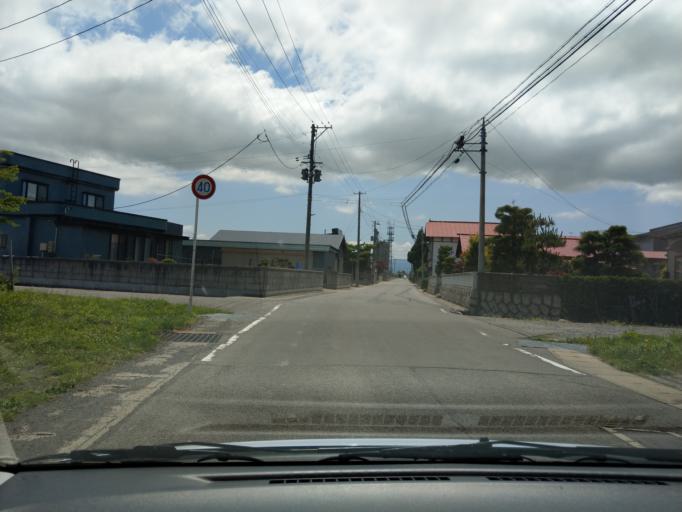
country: JP
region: Aomori
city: Kuroishi
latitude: 40.6771
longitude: 140.5593
